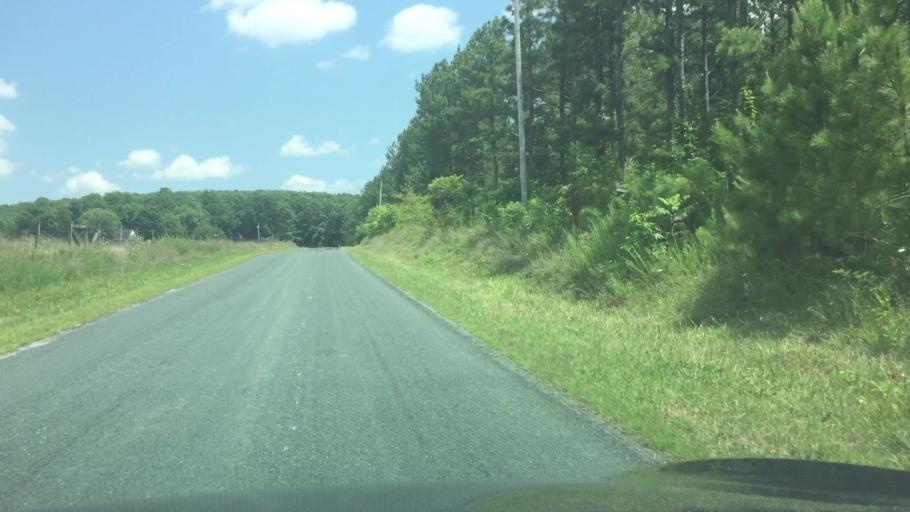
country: US
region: Virginia
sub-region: Appomattox County
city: Appomattox
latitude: 37.3215
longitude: -78.8549
